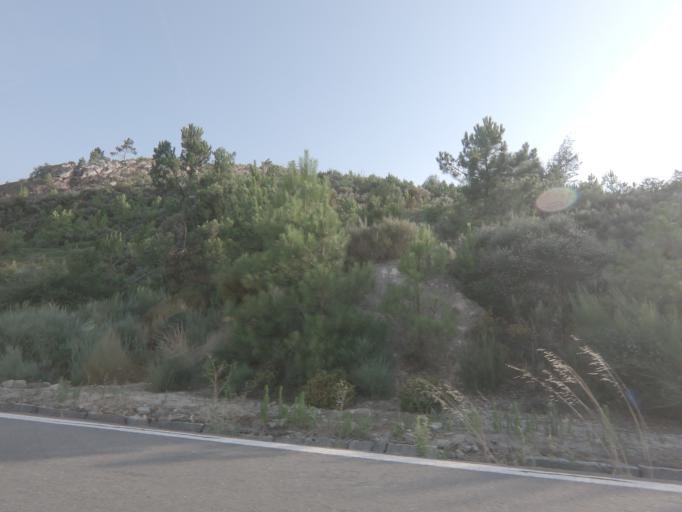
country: PT
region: Viseu
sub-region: Tabuaco
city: Tabuaco
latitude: 41.1181
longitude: -7.5803
